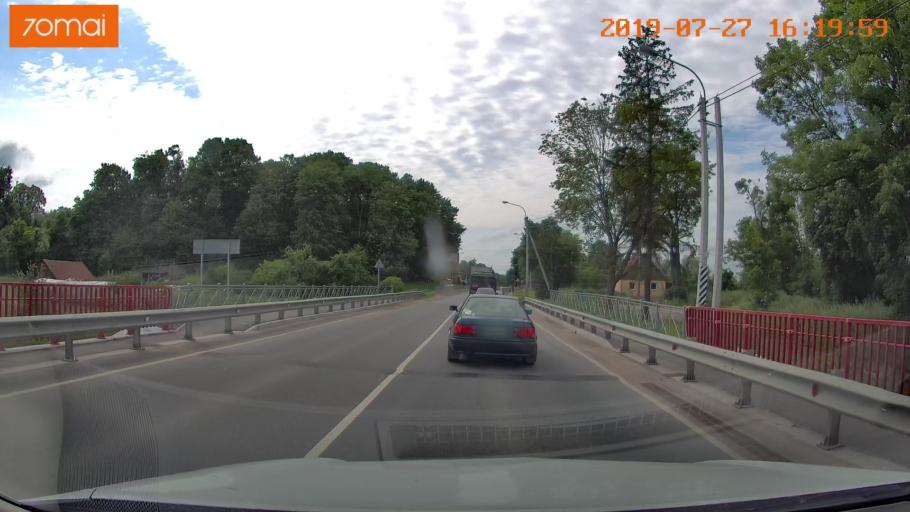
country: RU
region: Kaliningrad
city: Chernyakhovsk
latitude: 54.6258
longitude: 21.5277
